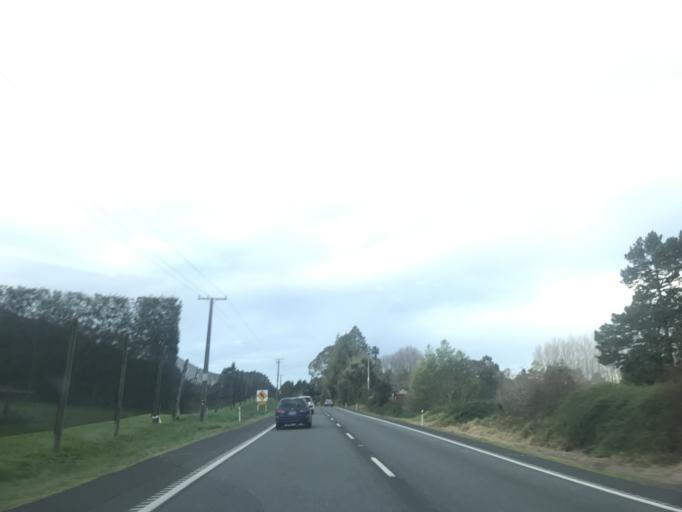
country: NZ
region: Bay of Plenty
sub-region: Western Bay of Plenty District
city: Katikati
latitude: -37.5026
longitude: 175.9248
